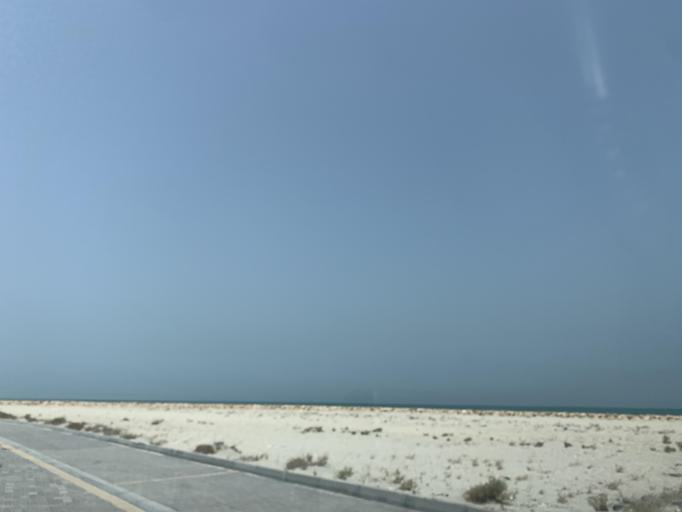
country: BH
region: Muharraq
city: Al Hadd
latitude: 26.2714
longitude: 50.6809
